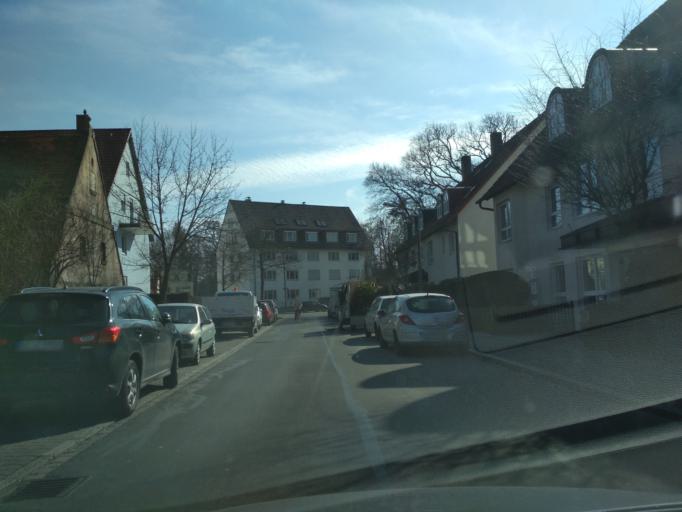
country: DE
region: Bavaria
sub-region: Regierungsbezirk Mittelfranken
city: Stein
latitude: 49.4052
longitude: 11.0413
